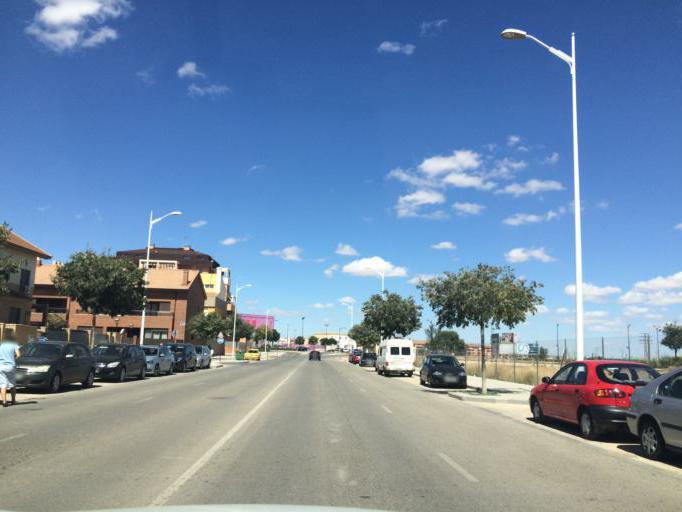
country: ES
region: Castille-La Mancha
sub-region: Provincia de Albacete
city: Albacete
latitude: 38.9832
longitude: -1.8421
